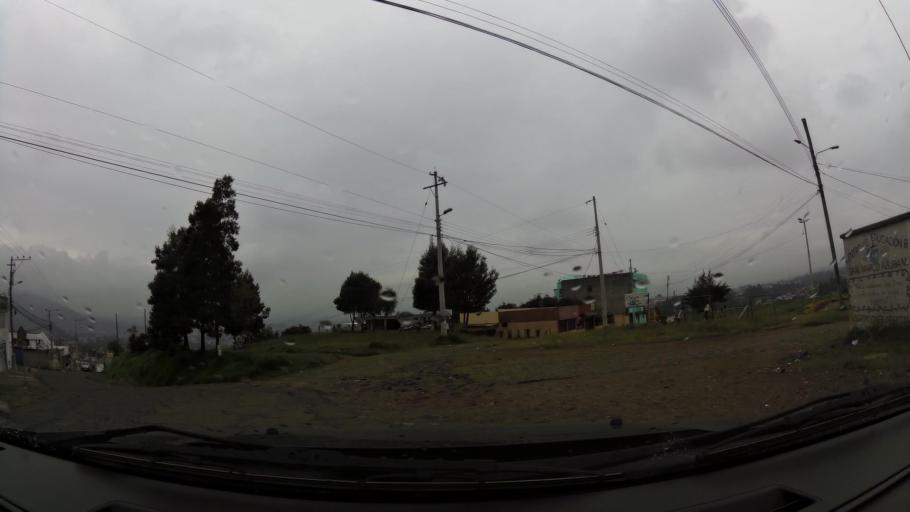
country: EC
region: Pichincha
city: Sangolqui
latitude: -0.2781
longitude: -78.4755
